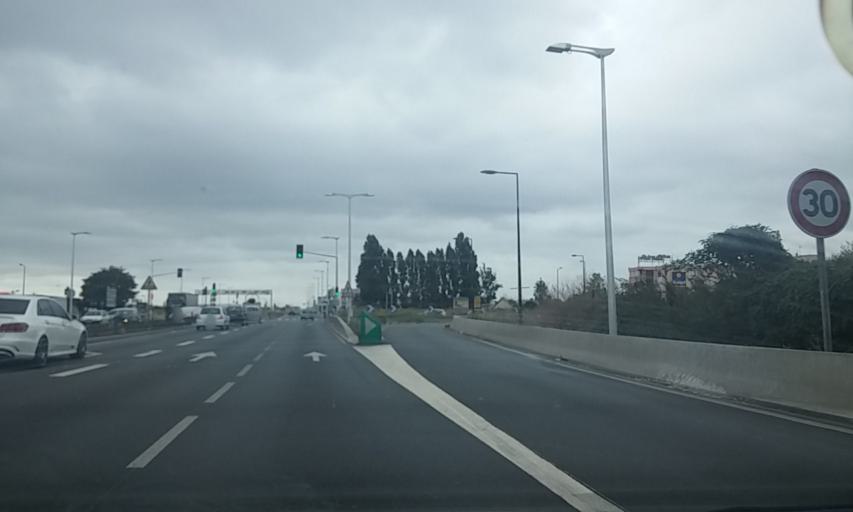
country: FR
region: Ile-de-France
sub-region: Departement de l'Essonne
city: Paray-Vieille-Poste
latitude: 48.7170
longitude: 2.3708
